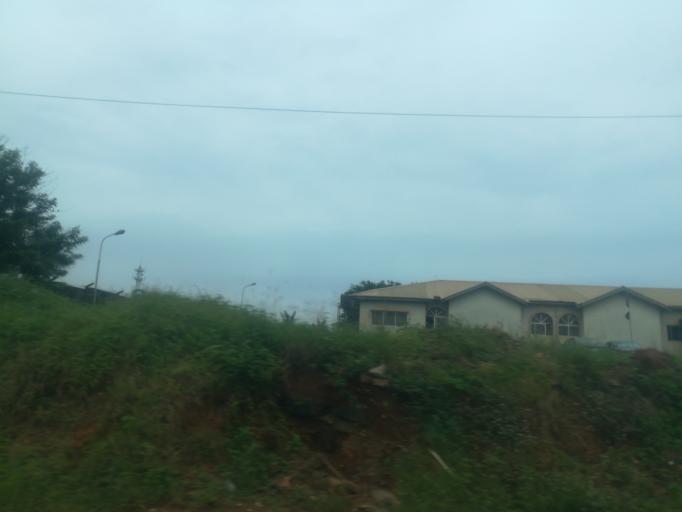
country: NG
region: Oyo
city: Ibadan
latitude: 7.3917
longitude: 3.9299
